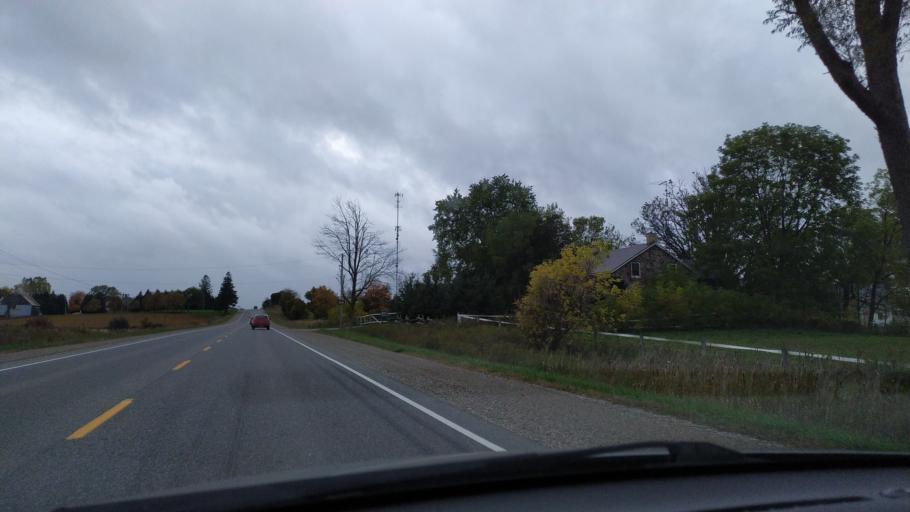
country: CA
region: Ontario
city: Stratford
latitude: 43.3694
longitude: -80.8141
